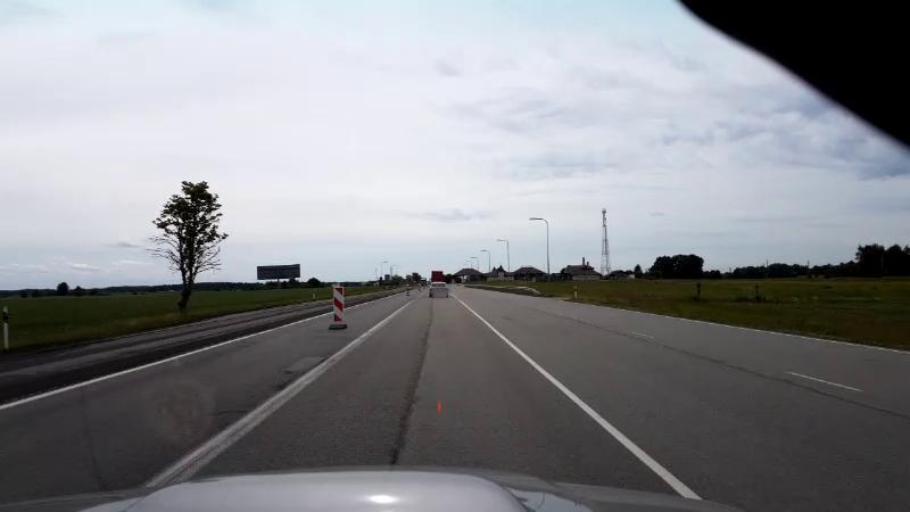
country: LV
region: Bauskas Rajons
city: Bauska
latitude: 56.2788
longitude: 24.3626
